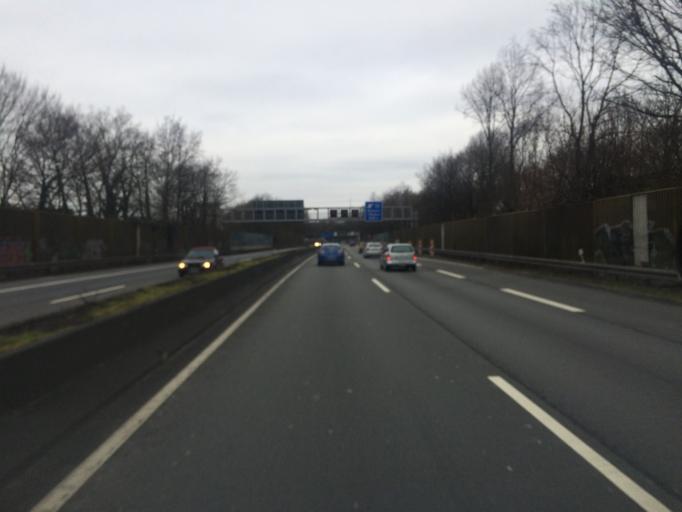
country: DE
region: North Rhine-Westphalia
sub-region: Regierungsbezirk Arnsberg
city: Bochum
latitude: 51.4948
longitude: 7.2500
